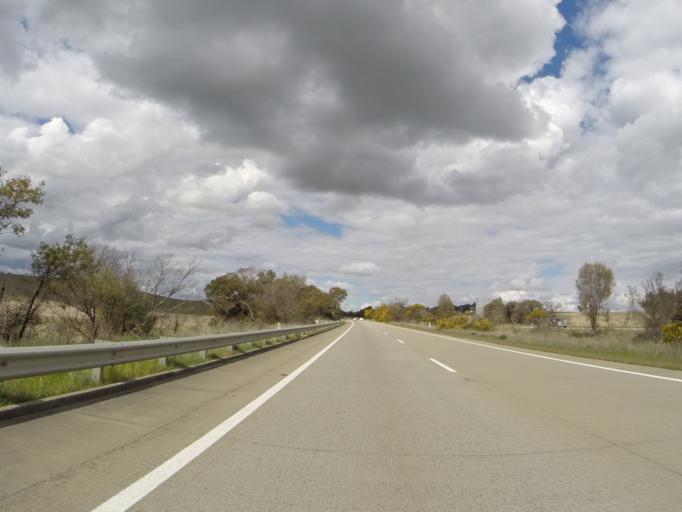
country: AU
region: New South Wales
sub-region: Yass Valley
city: Gundaroo
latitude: -34.7983
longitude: 149.2818
